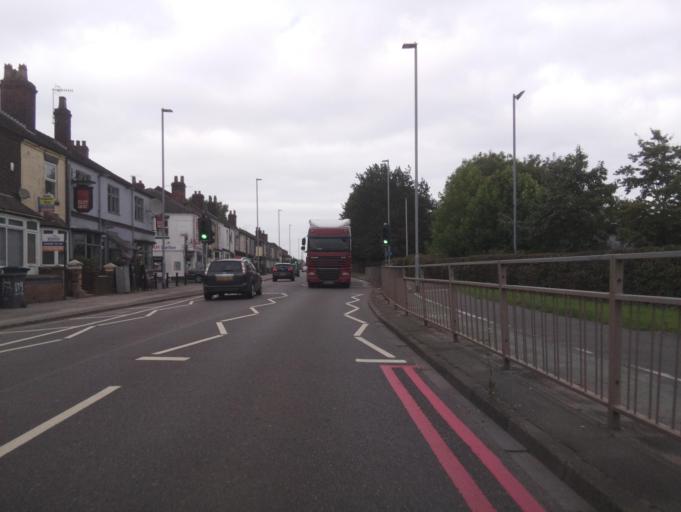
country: GB
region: England
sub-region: Stoke-on-Trent
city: Stoke-on-Trent
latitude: 53.0099
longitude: -2.1754
